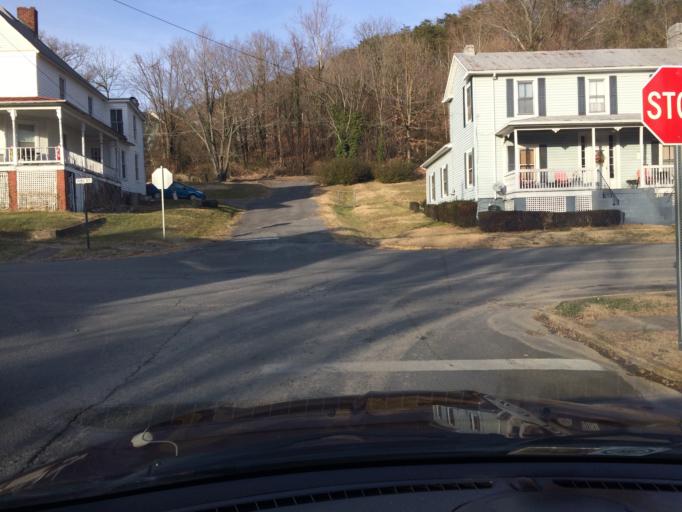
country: US
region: Virginia
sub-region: Alleghany County
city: Clifton Forge
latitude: 37.8175
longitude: -79.8220
